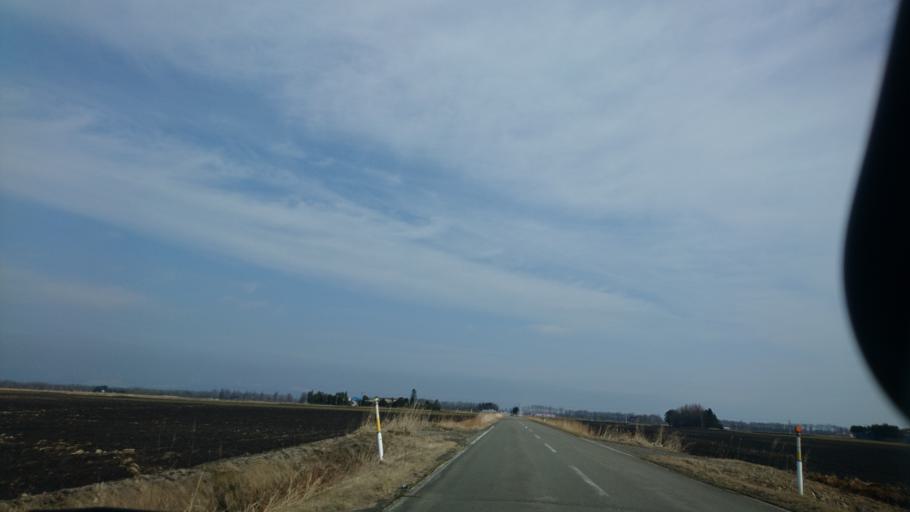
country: JP
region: Hokkaido
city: Otofuke
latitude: 43.0657
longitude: 143.2367
